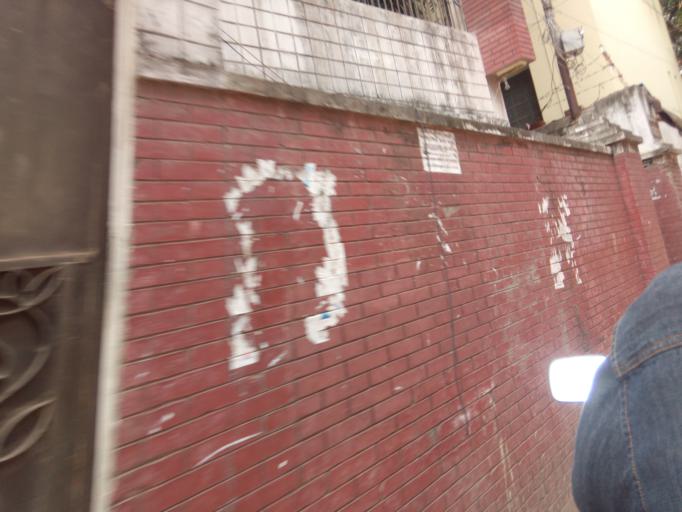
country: BD
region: Dhaka
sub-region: Dhaka
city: Dhaka
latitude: 23.7004
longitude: 90.4242
